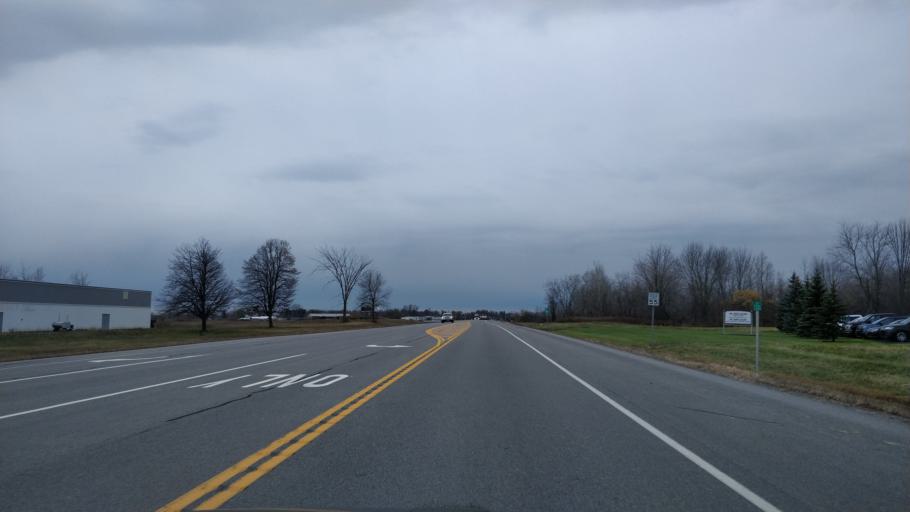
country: US
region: New York
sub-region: St. Lawrence County
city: Ogdensburg
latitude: 44.6981
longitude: -75.4649
